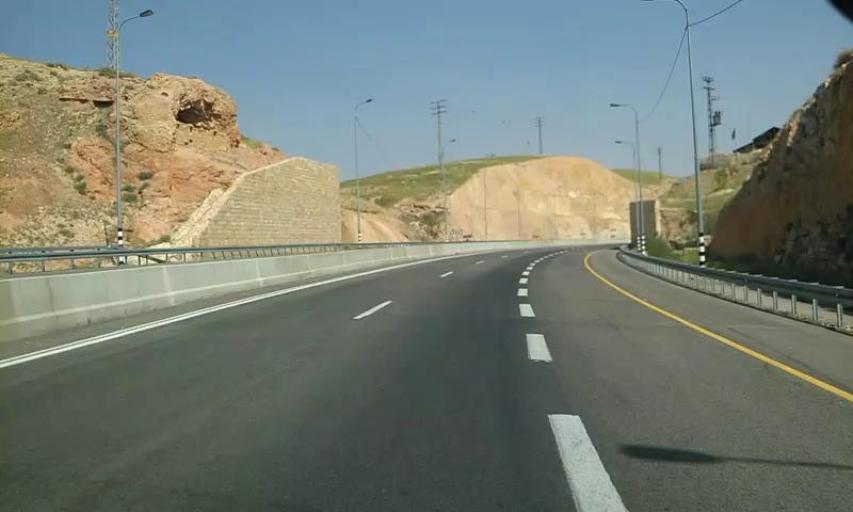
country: PS
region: West Bank
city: Hizma
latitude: 31.8171
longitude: 35.3586
